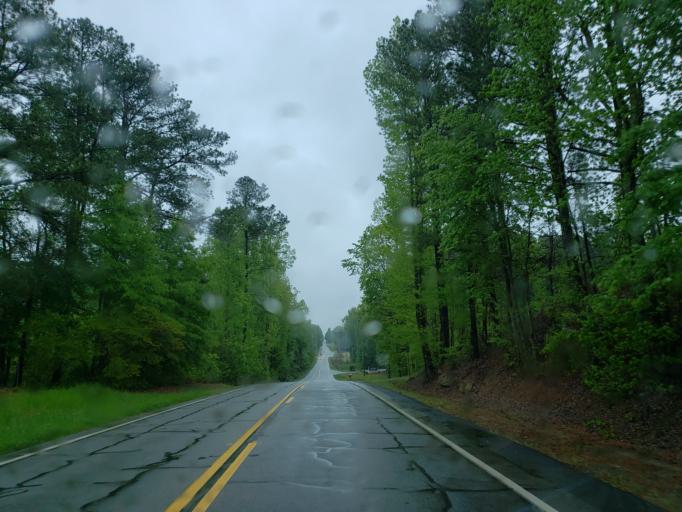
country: US
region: Georgia
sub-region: Paulding County
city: Dallas
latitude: 33.8311
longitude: -84.8718
